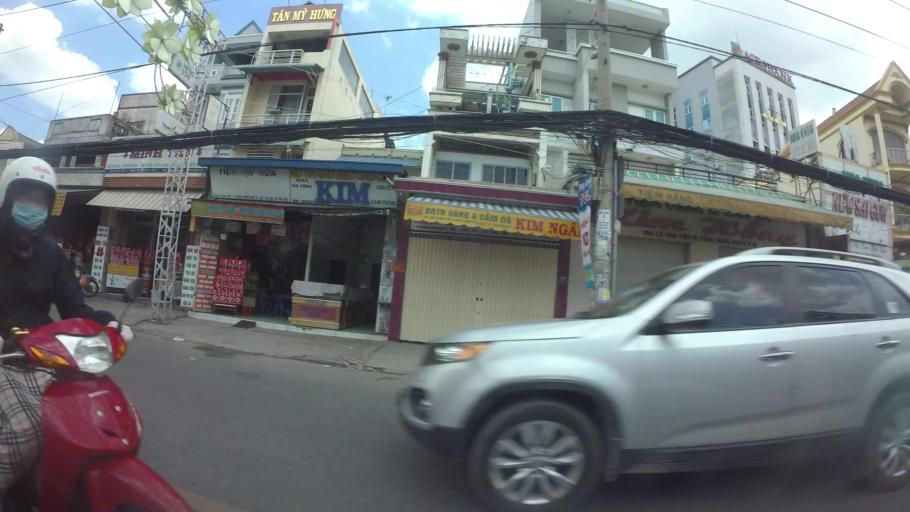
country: VN
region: Ho Chi Minh City
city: Thu Duc
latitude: 10.8439
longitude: 106.7826
